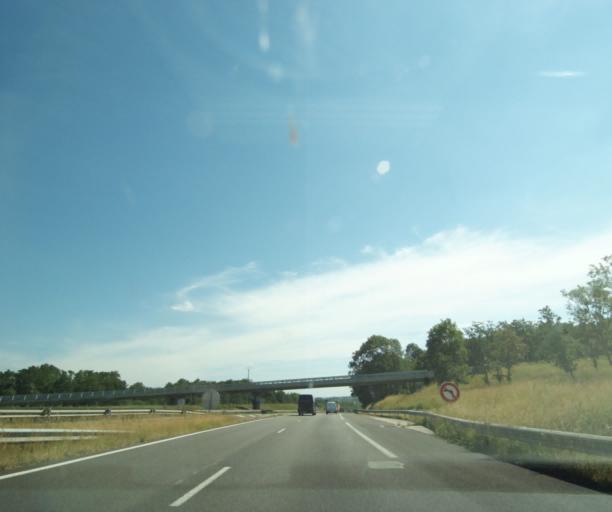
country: FR
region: Lorraine
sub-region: Departement de Meurthe-et-Moselle
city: Dommartin-les-Toul
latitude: 48.6524
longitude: 5.8827
